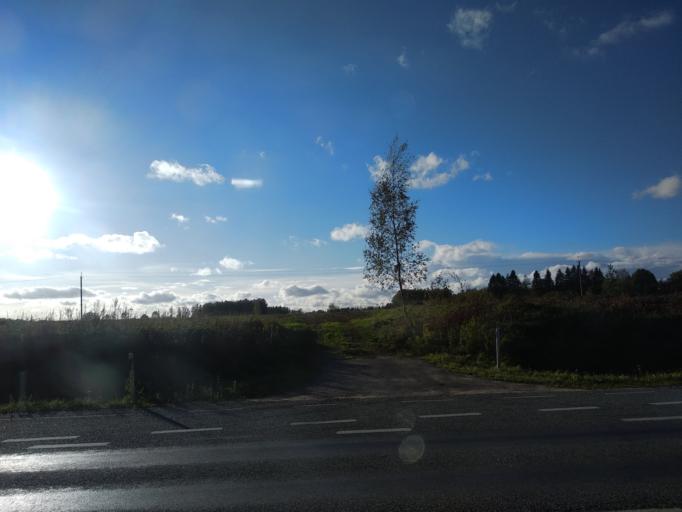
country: EE
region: Polvamaa
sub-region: Polva linn
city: Polva
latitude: 58.0396
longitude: 27.0660
